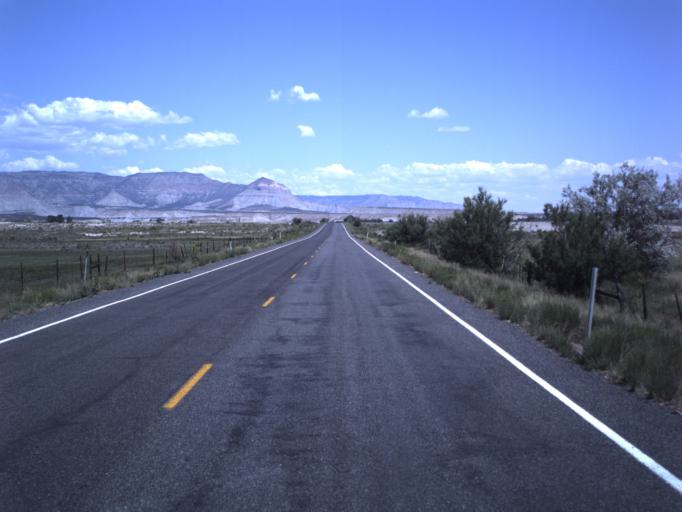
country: US
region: Utah
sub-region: Emery County
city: Orangeville
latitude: 39.1957
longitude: -111.0478
